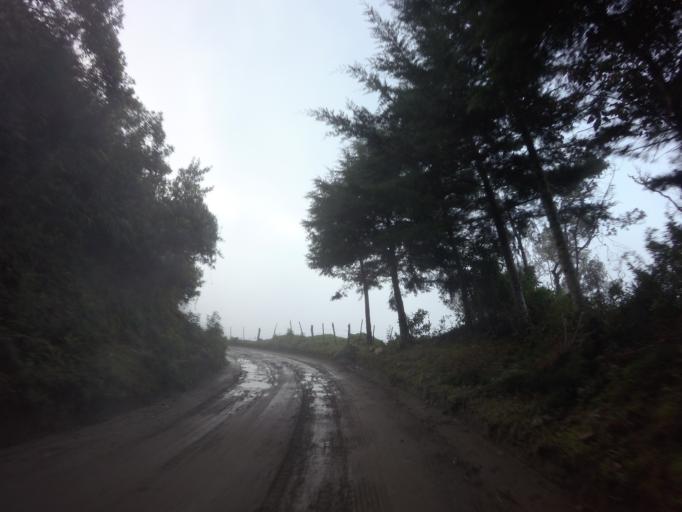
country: CO
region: Caldas
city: Pensilvania
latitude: 5.4183
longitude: -75.1285
